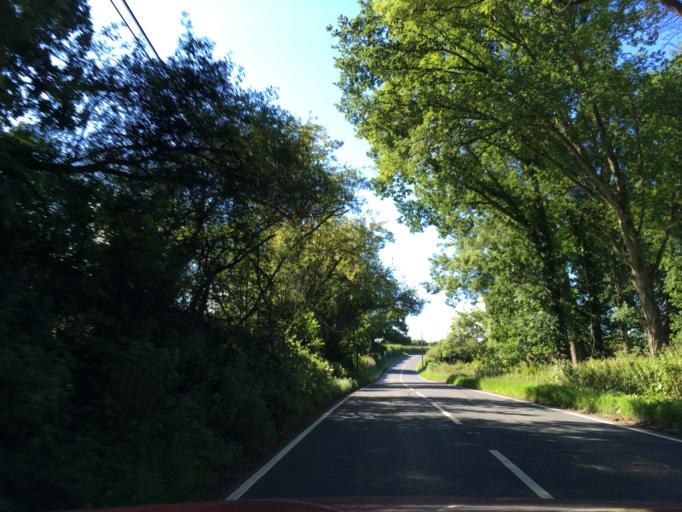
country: GB
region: England
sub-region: Herefordshire
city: Yatton
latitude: 51.9706
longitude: -2.5523
